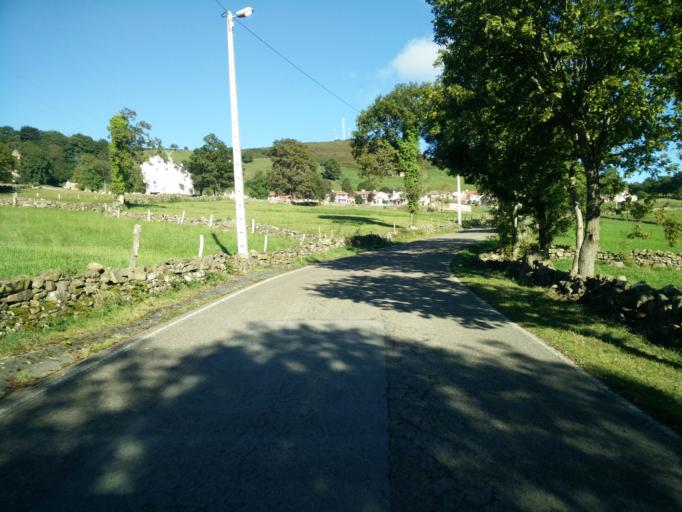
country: ES
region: Cantabria
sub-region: Provincia de Cantabria
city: San Pedro del Romeral
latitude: 43.1150
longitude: -3.8144
